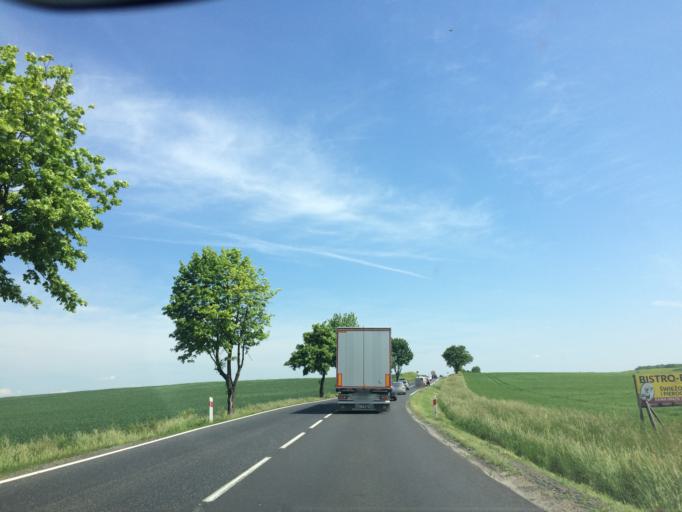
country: PL
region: Lower Silesian Voivodeship
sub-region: Powiat wroclawski
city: Gniechowice
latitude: 50.9670
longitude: 16.7999
